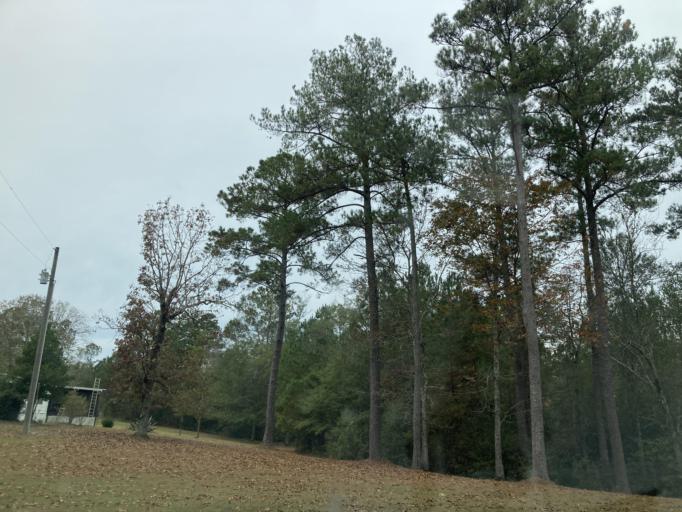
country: US
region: Mississippi
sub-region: Lamar County
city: Lumberton
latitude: 31.0569
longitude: -89.5159
